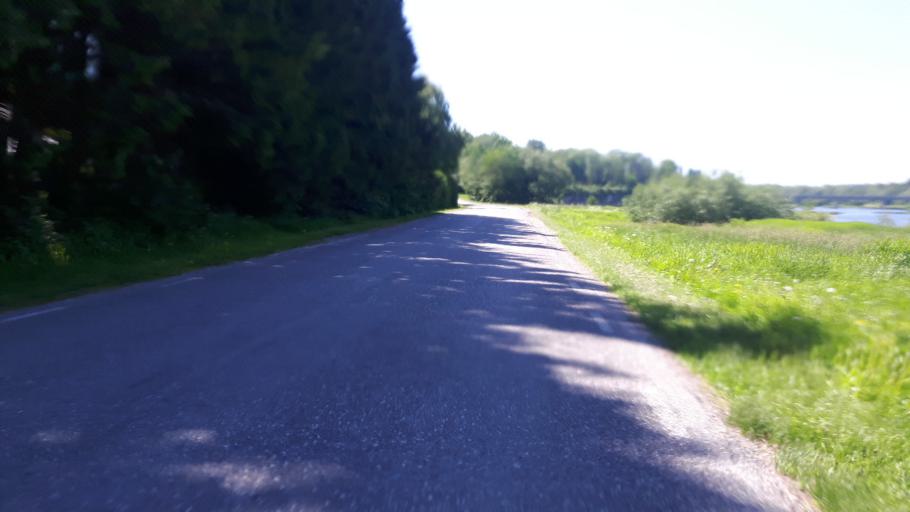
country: EE
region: Paernumaa
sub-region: Tootsi vald
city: Tootsi
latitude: 58.4850
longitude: 24.8260
